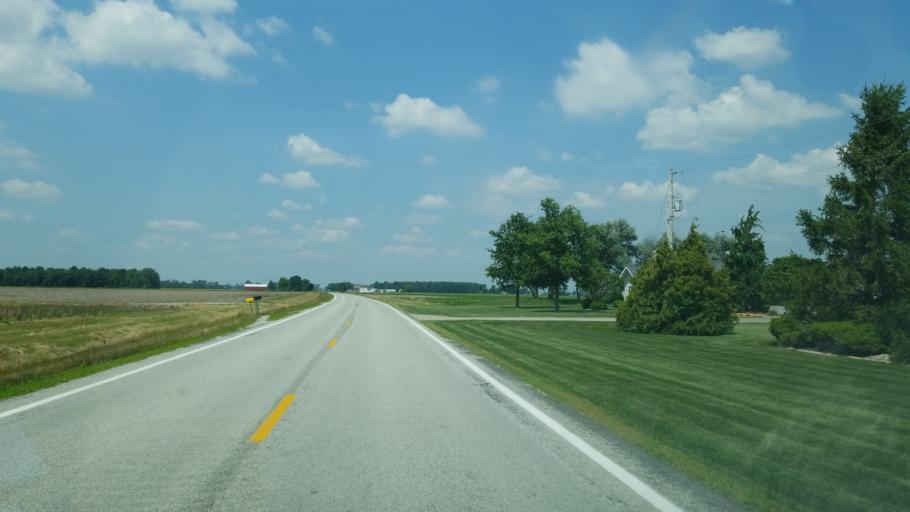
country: US
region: Ohio
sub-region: Henry County
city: Deshler
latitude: 41.2834
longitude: -84.0024
